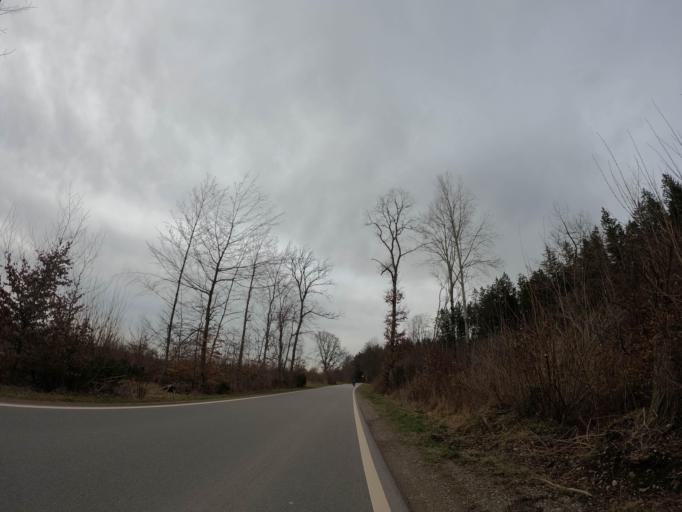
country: DE
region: Bavaria
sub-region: Upper Bavaria
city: Oberhaching
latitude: 48.0131
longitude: 11.5686
